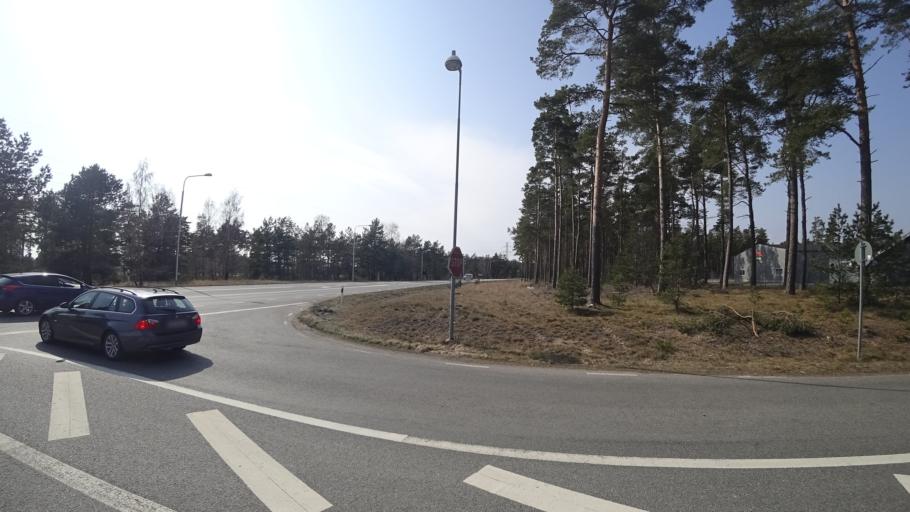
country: SE
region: Skane
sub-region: Kristianstads Kommun
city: Ahus
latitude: 55.9288
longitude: 14.2736
